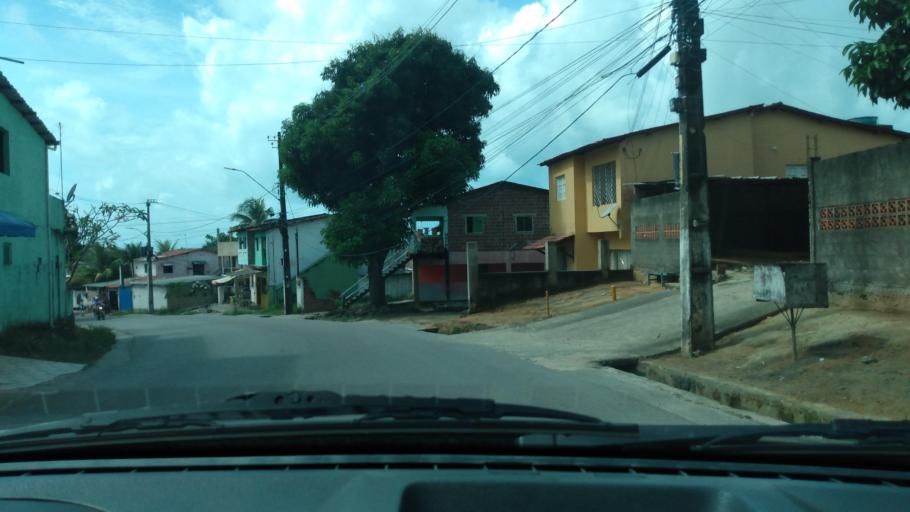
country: BR
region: Pernambuco
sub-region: Cabo De Santo Agostinho
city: Cabo
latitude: -8.3429
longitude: -34.9557
